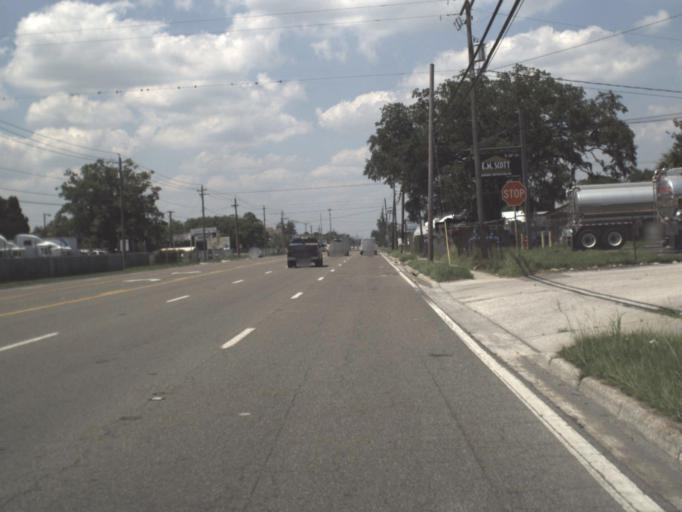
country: US
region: Florida
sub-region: Hillsborough County
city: Palm River-Clair Mel
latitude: 27.9321
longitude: -82.4018
